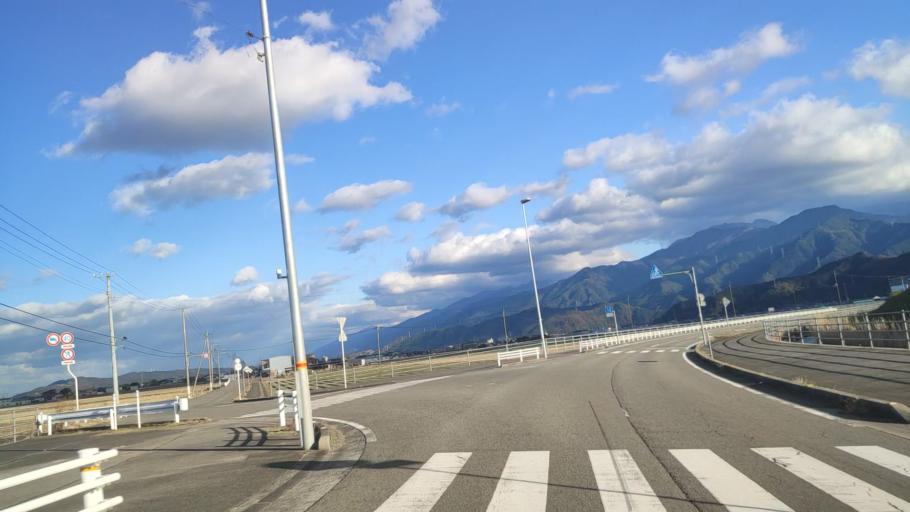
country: JP
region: Ehime
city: Saijo
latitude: 33.9093
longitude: 133.1409
